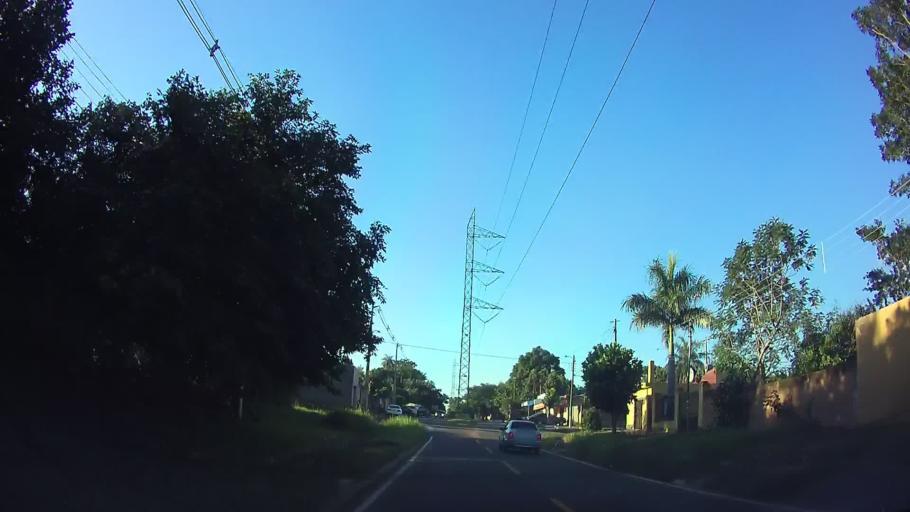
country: PY
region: Central
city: San Lorenzo
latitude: -25.2799
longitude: -57.4650
